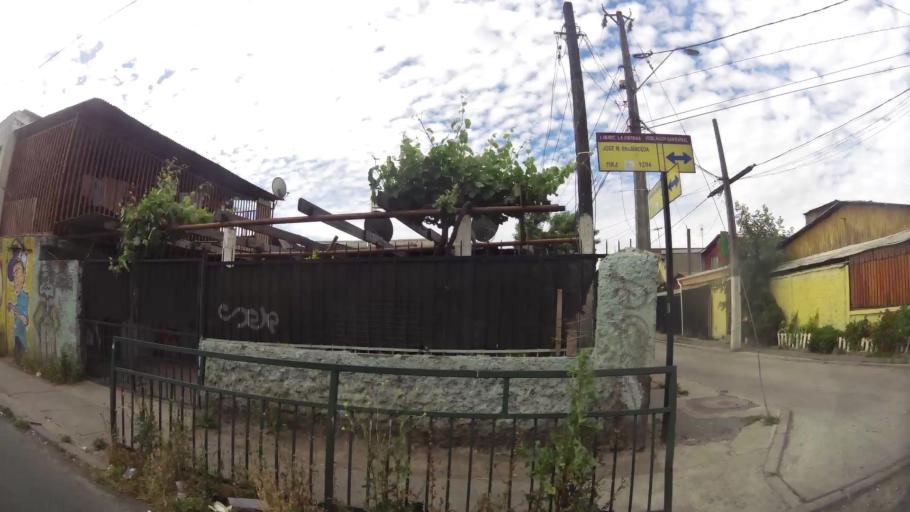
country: CL
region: Santiago Metropolitan
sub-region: Provincia de Santiago
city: La Pintana
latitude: -33.5789
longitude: -70.6400
